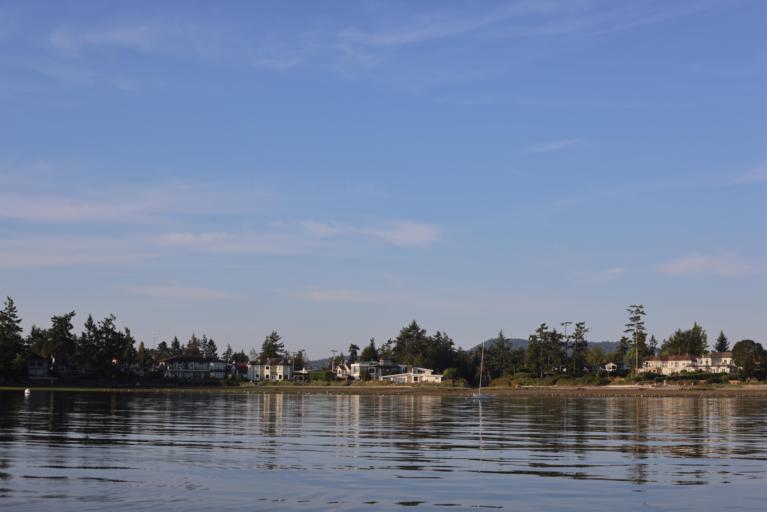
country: CA
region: British Columbia
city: North Saanich
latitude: 48.6637
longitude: -123.3993
